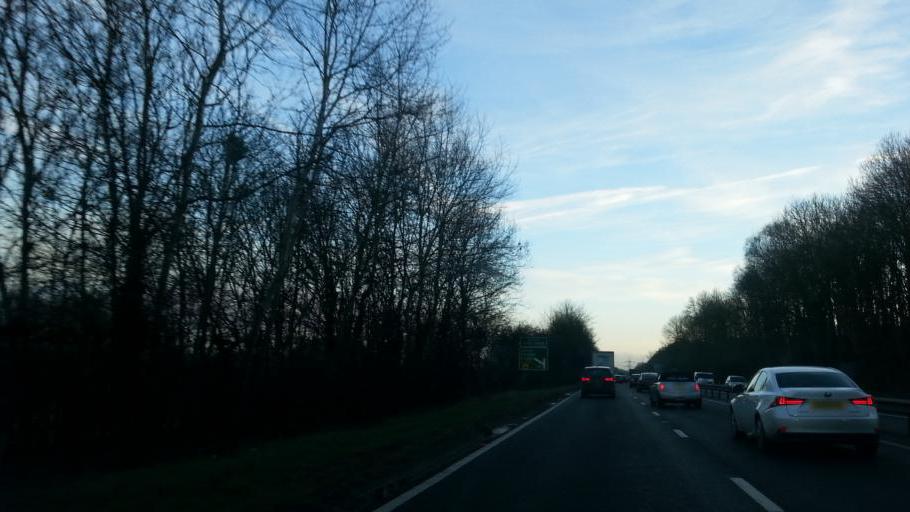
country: GB
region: England
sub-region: Oxfordshire
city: Yarnton
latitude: 51.7671
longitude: -1.3006
